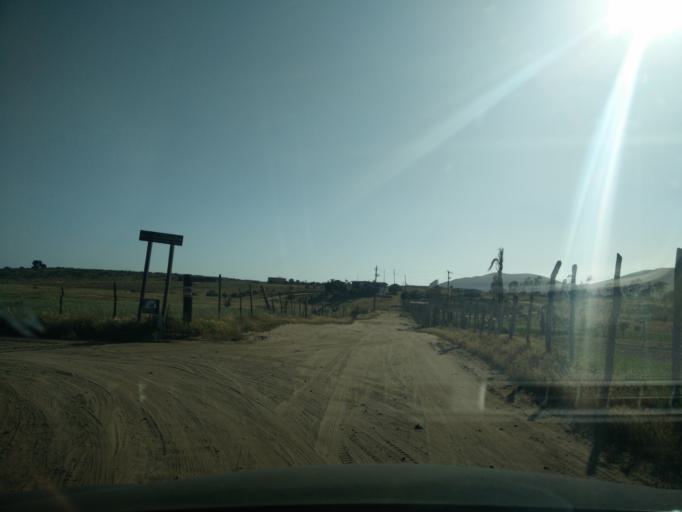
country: MX
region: Baja California
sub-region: Ensenada
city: Rancho Verde
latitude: 32.0467
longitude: -116.6479
